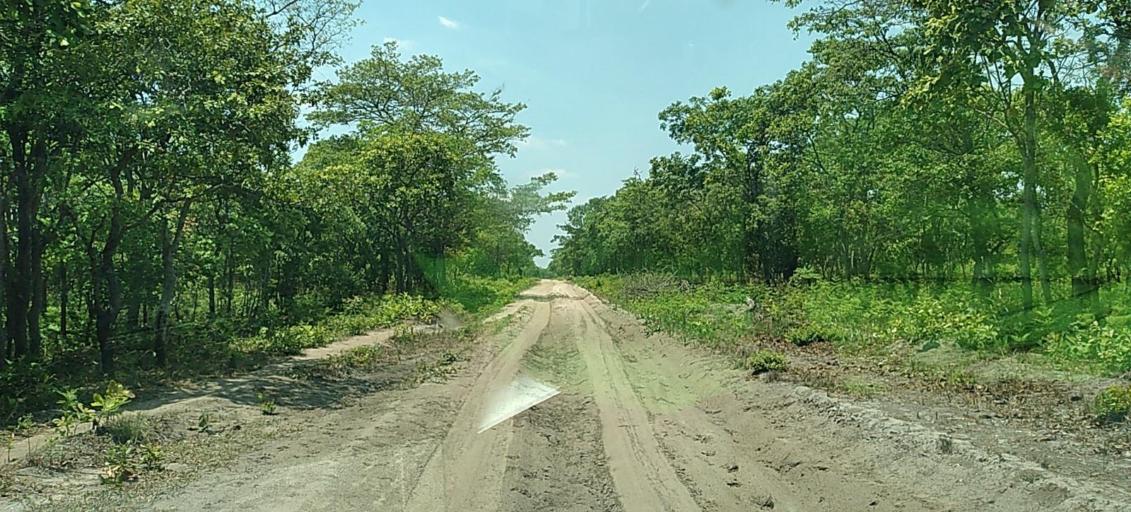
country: CD
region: Katanga
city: Kolwezi
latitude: -11.3420
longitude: 25.2182
